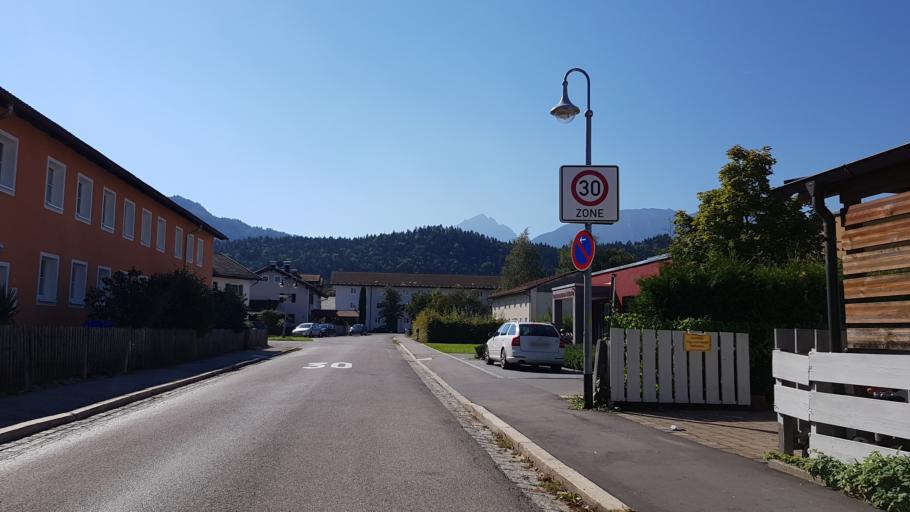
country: DE
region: Bavaria
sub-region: Swabia
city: Fuessen
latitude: 47.5730
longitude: 10.6805
